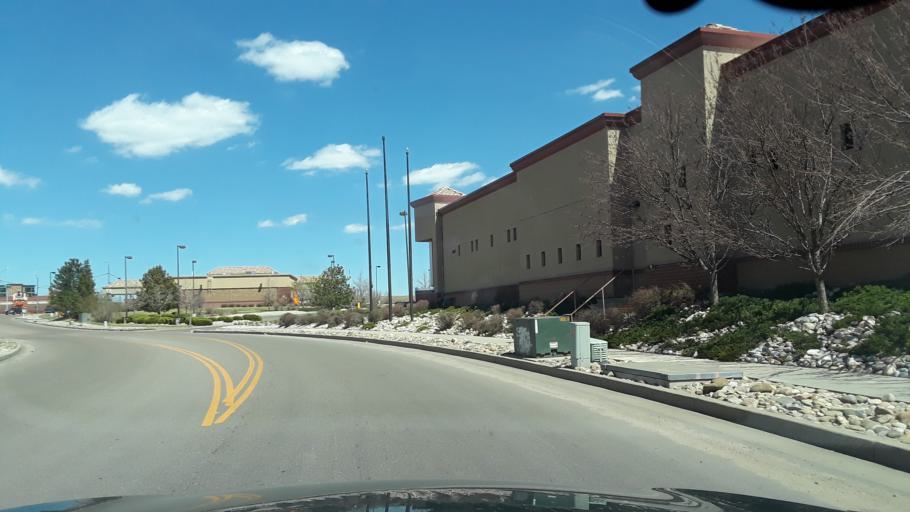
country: US
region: Colorado
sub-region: El Paso County
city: Cimarron Hills
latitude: 38.8691
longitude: -104.7164
